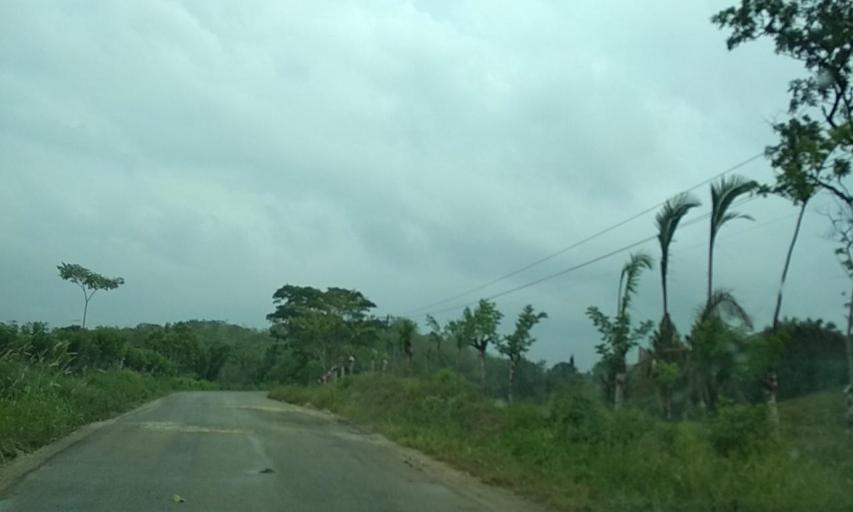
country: MX
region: Tabasco
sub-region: Huimanguillo
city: Francisco Rueda
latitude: 17.5849
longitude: -94.0925
